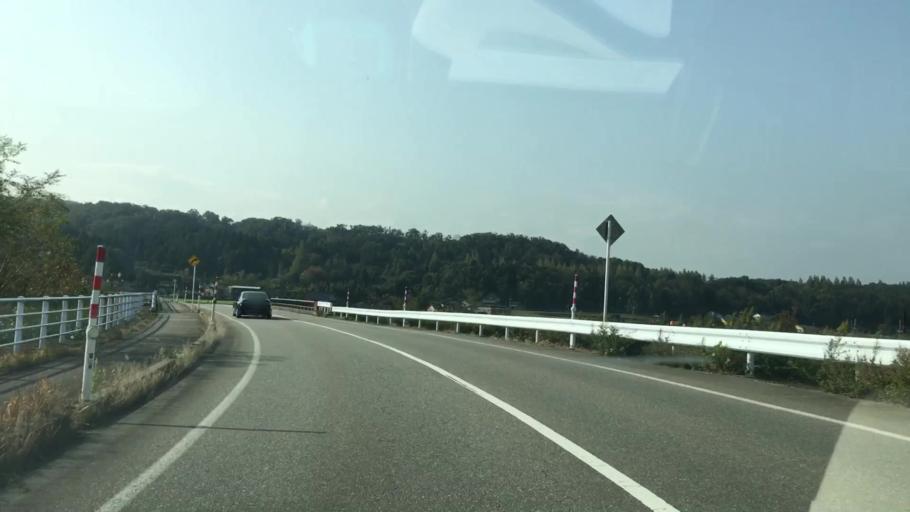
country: JP
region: Toyama
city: Toyama-shi
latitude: 36.6029
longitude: 137.2527
